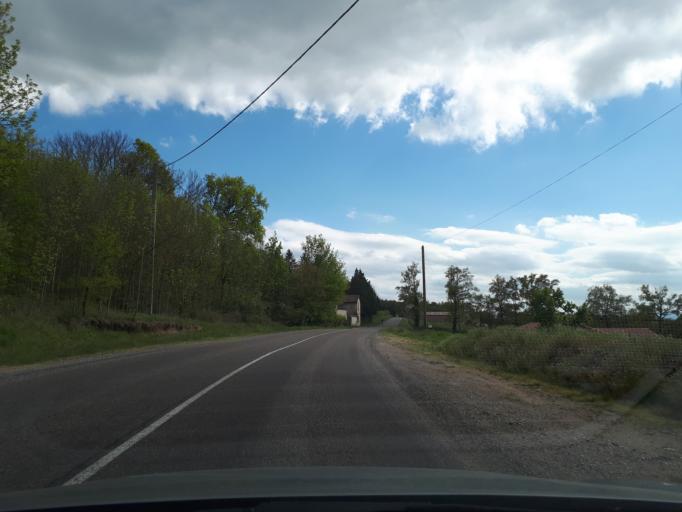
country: FR
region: Rhone-Alpes
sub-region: Departement de la Loire
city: Bellegarde-en-Forez
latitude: 45.6949
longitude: 4.3032
